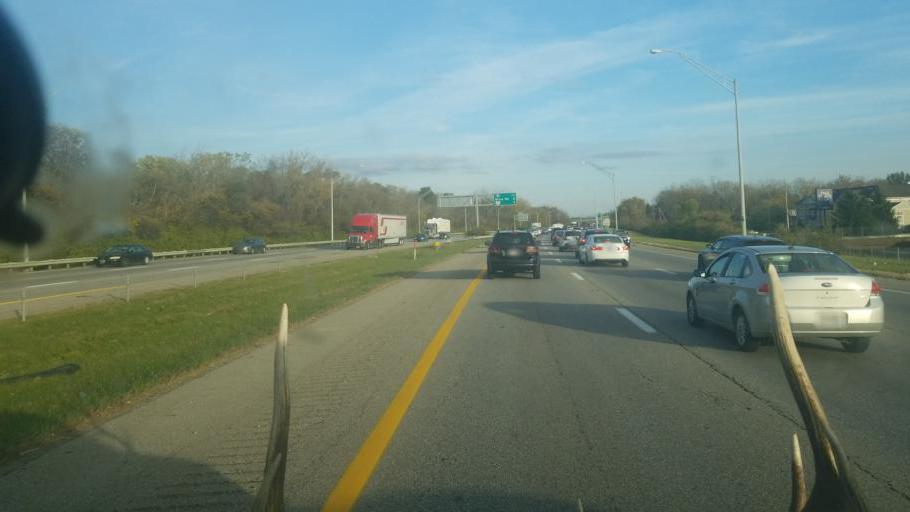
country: US
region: Ohio
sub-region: Franklin County
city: Blacklick Estates
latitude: 39.9369
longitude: -82.8706
